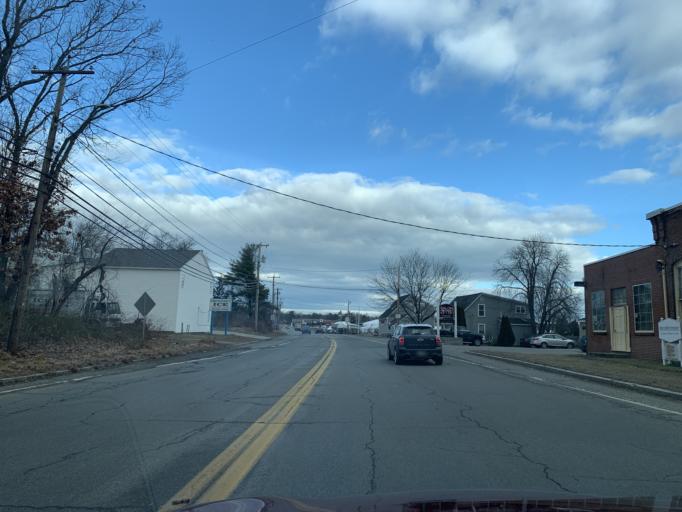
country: US
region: Massachusetts
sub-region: Essex County
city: Newburyport
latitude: 42.8183
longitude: -70.8697
